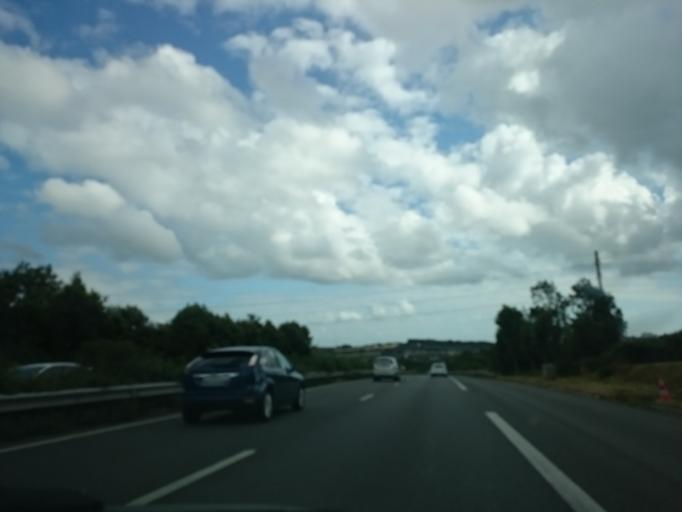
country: FR
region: Brittany
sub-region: Departement du Finistere
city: Gouesnou
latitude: 48.4259
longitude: -4.4371
